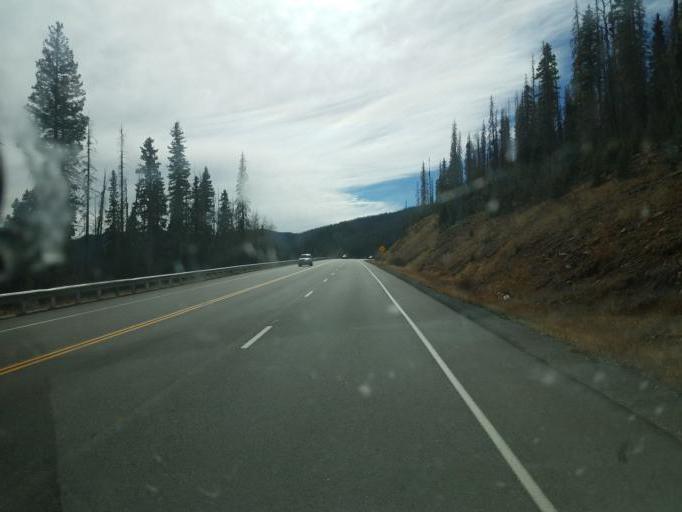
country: US
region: Colorado
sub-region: Archuleta County
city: Pagosa Springs
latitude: 37.5107
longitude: -106.7738
